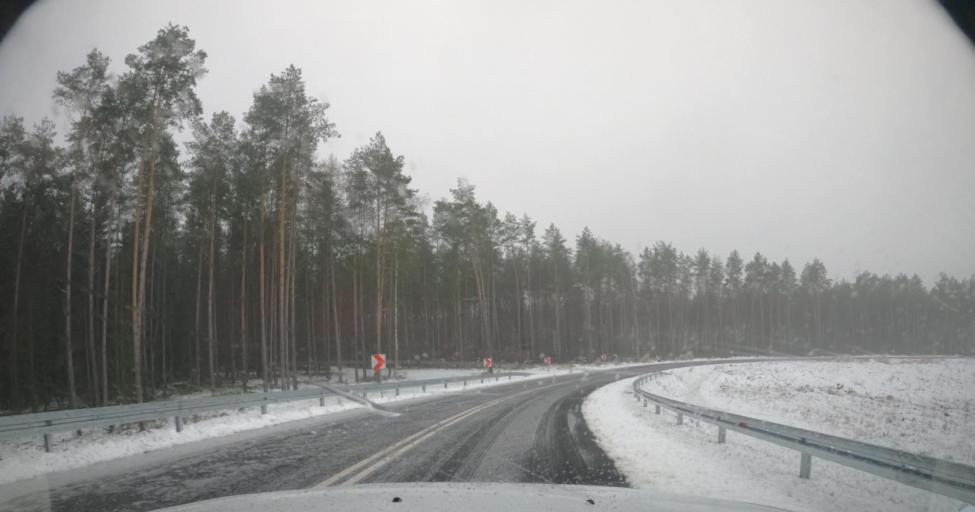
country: PL
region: West Pomeranian Voivodeship
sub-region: Powiat goleniowski
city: Goleniow
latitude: 53.6582
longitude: 14.8172
